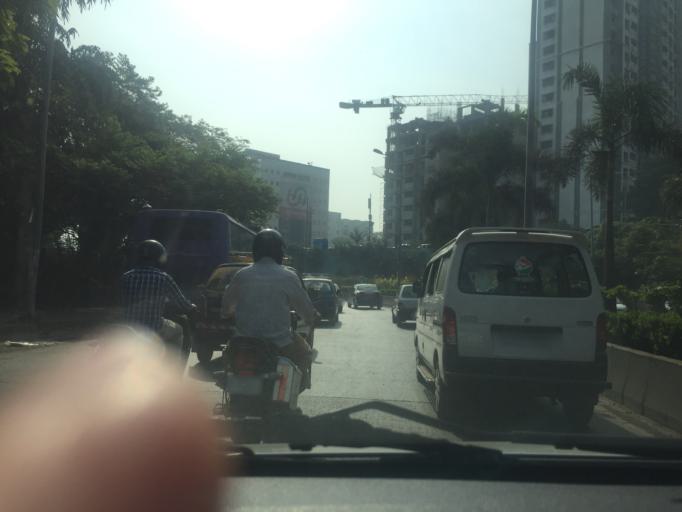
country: IN
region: Maharashtra
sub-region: Mumbai Suburban
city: Powai
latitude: 19.1253
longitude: 72.8950
